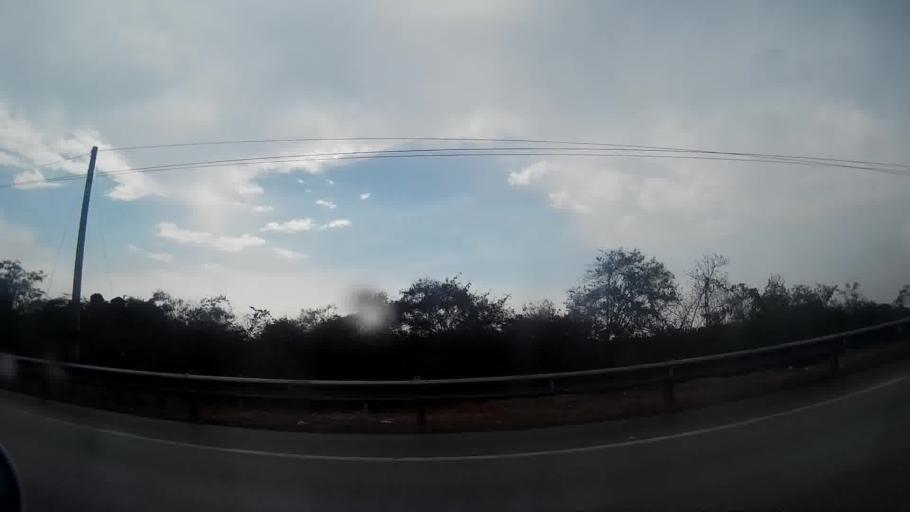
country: CO
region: Magdalena
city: Cienaga
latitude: 11.0179
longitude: -74.2134
